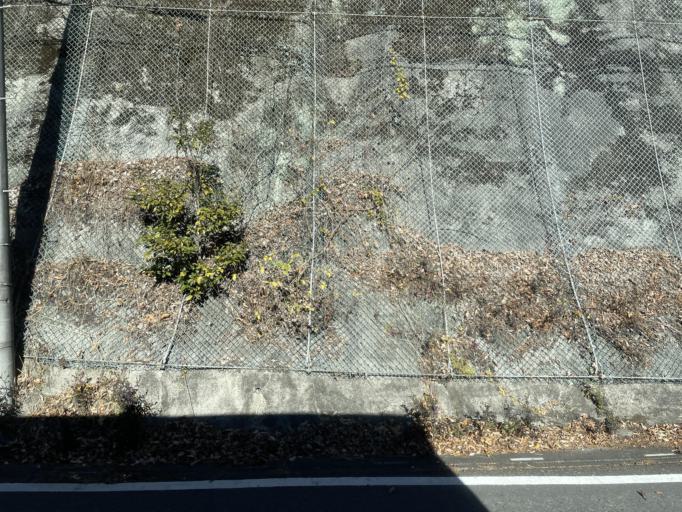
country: JP
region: Saitama
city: Yorii
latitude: 36.0645
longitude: 139.1849
